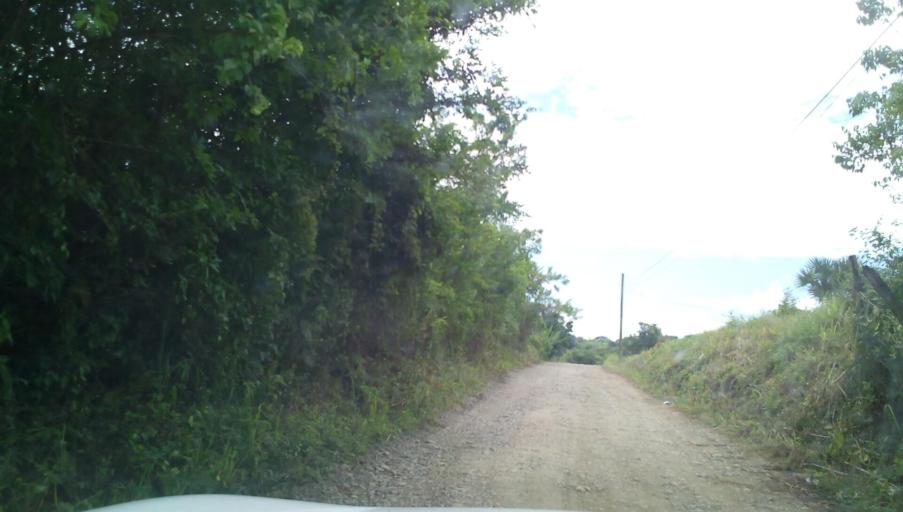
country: MX
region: Veracruz
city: Tepetzintla
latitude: 21.1562
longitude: -97.8526
